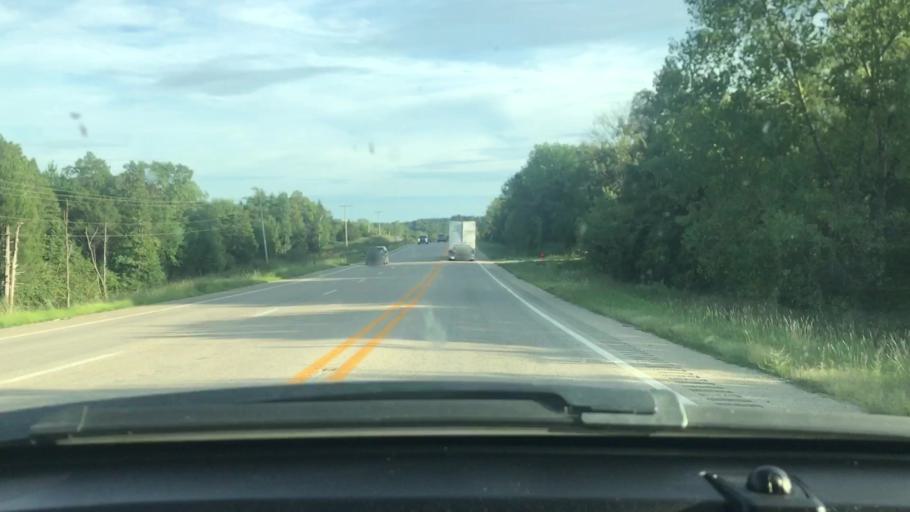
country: US
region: Arkansas
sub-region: Lawrence County
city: Hoxie
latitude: 36.1467
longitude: -91.1595
